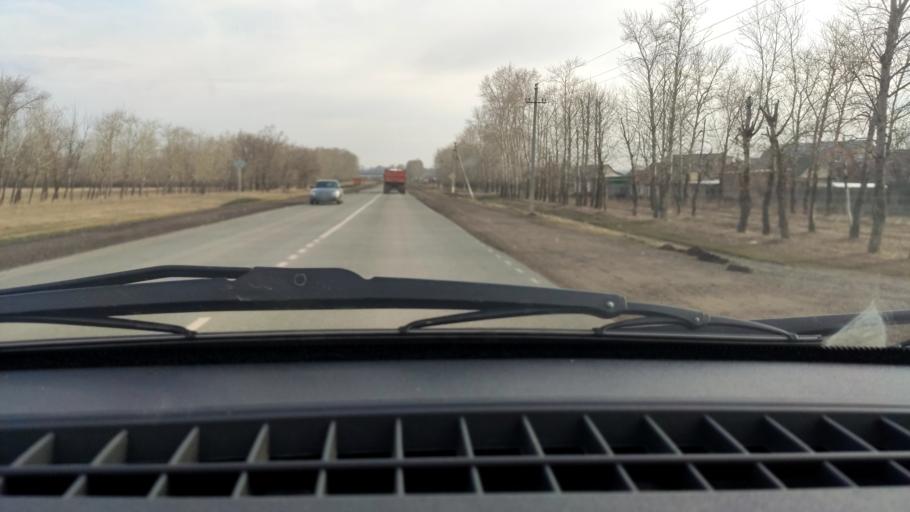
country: RU
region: Bashkortostan
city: Davlekanovo
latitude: 54.3882
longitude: 55.2005
